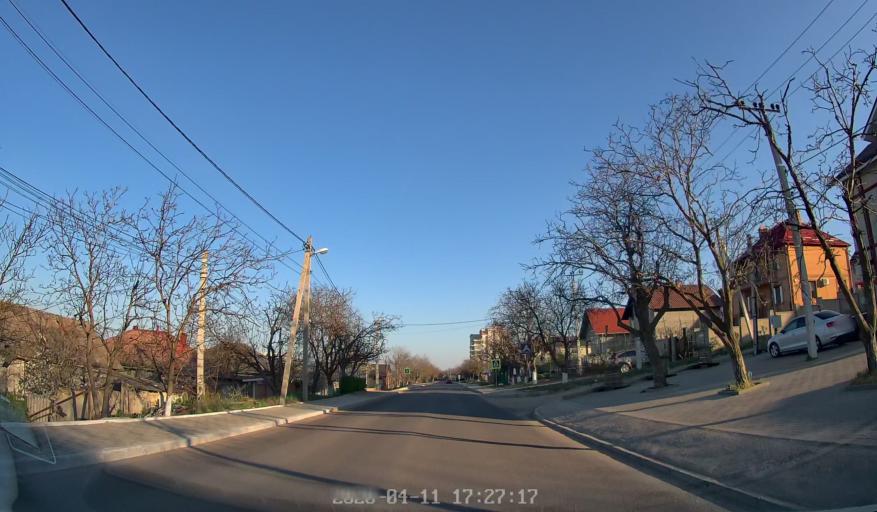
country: MD
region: Laloveni
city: Ialoveni
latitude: 47.0096
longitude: 28.7619
